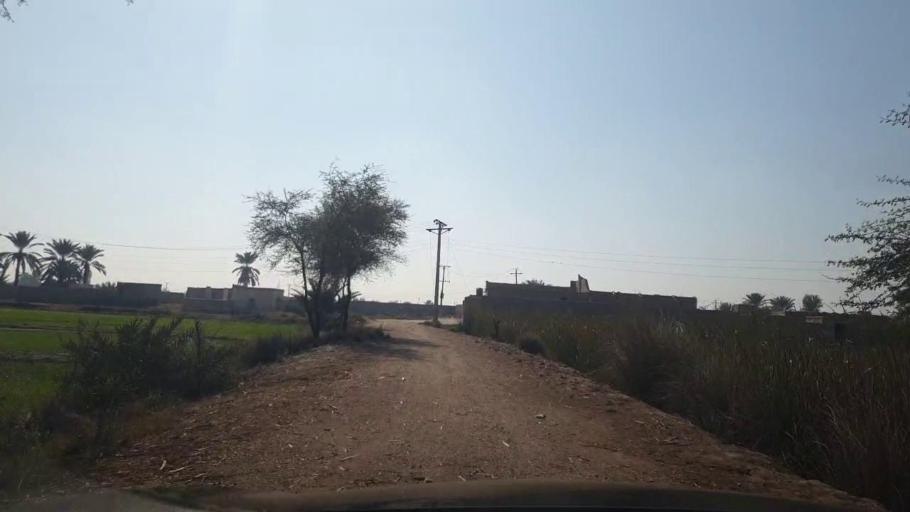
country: PK
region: Sindh
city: Ghotki
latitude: 27.9836
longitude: 69.3560
